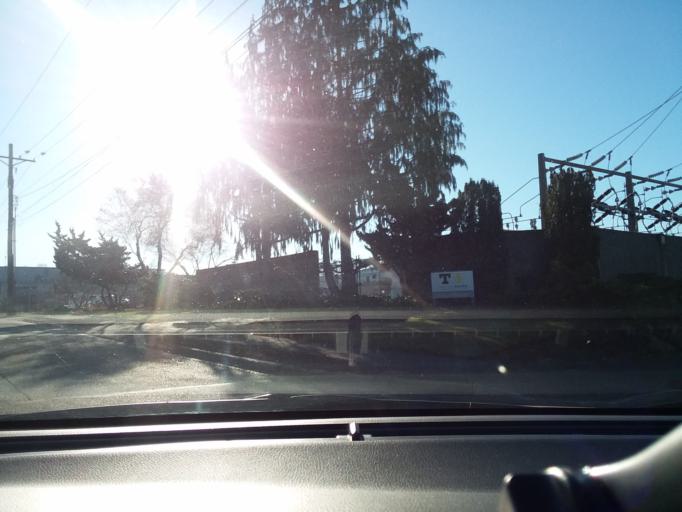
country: US
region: Washington
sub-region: Pierce County
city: Tacoma
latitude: 47.2262
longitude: -122.4763
